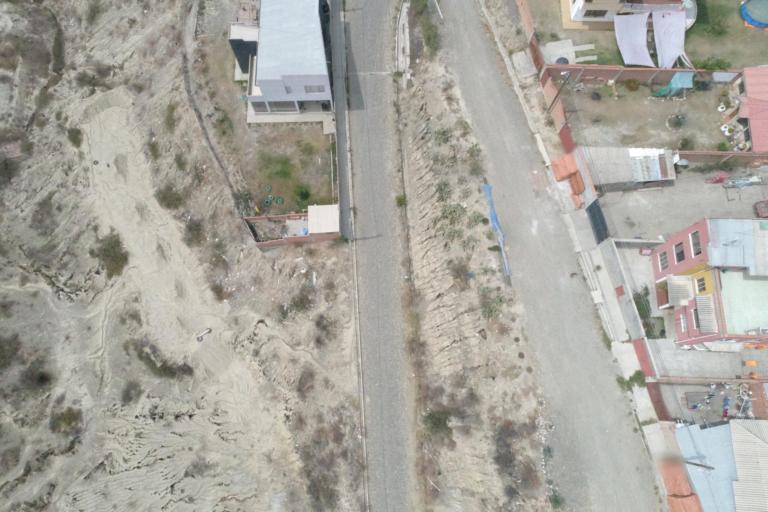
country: BO
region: La Paz
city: La Paz
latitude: -16.5996
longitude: -68.0700
